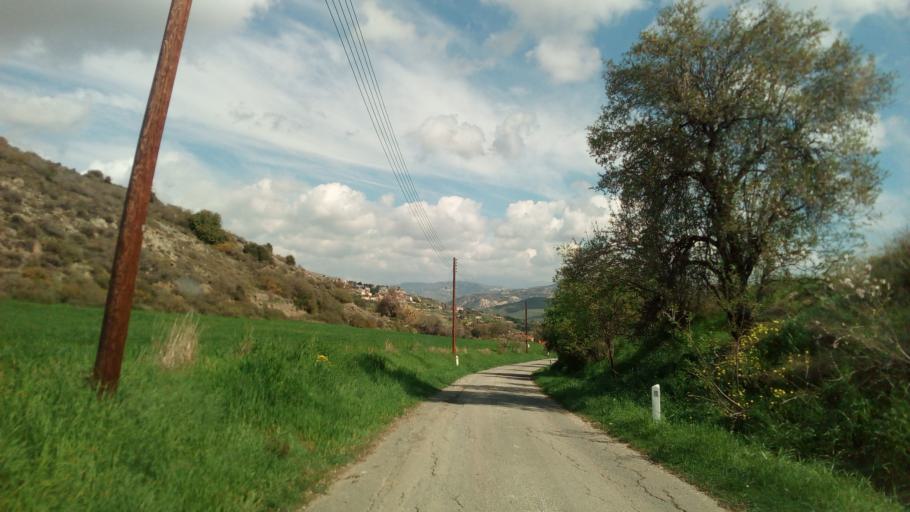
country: CY
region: Pafos
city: Mesogi
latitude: 34.7704
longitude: 32.5611
